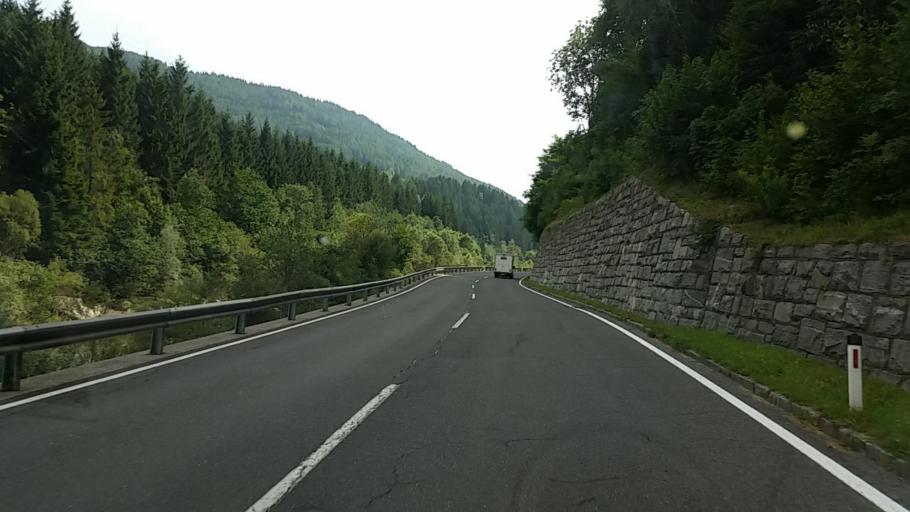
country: AT
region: Carinthia
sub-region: Politischer Bezirk Spittal an der Drau
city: Gmuend
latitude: 46.8955
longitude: 13.5267
